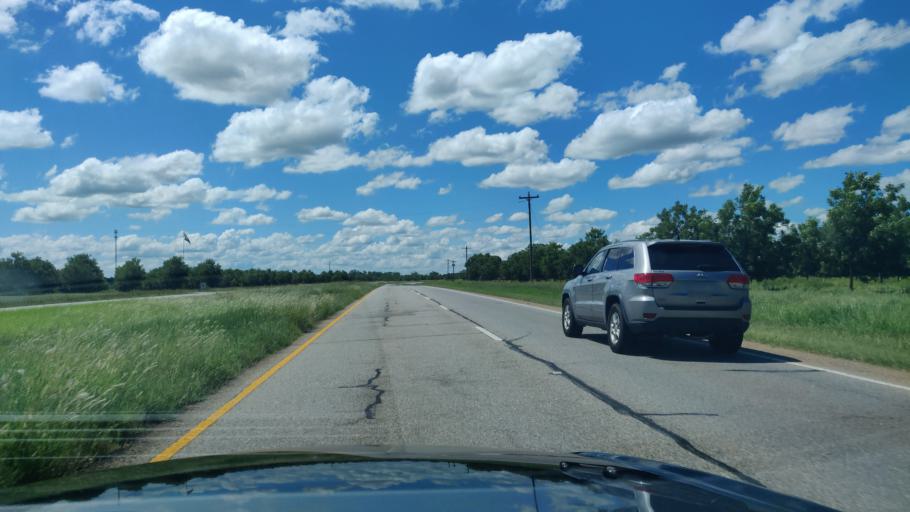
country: US
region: Georgia
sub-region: Webster County
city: Preston
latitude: 31.9372
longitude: -84.5661
